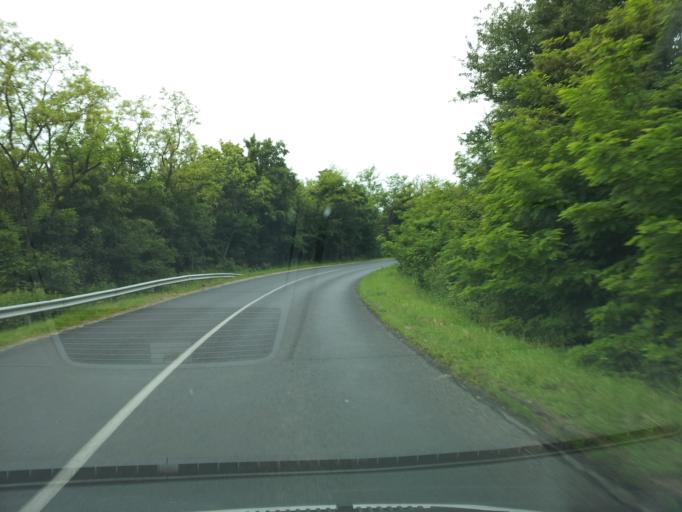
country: HU
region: Pest
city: Csobanka
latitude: 47.6668
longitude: 18.9602
